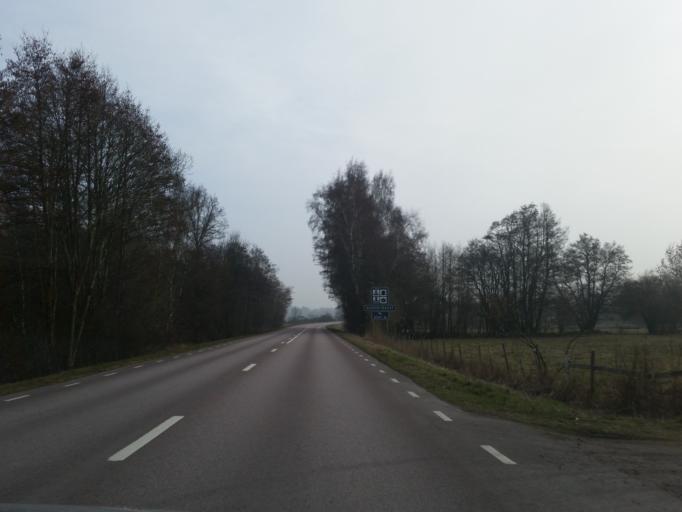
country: SE
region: Kalmar
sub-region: Borgholms Kommun
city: Borgholm
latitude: 57.1790
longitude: 17.0286
